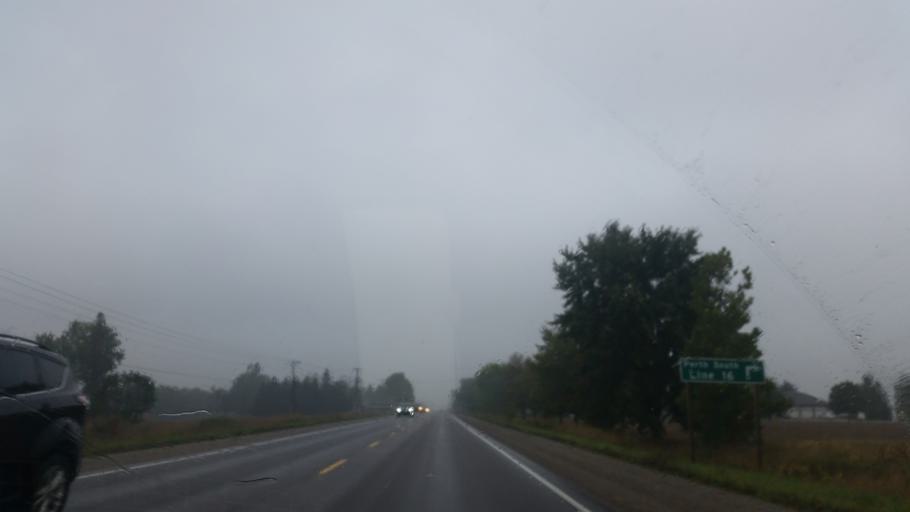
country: CA
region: Ontario
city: Stratford
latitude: 43.2959
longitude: -81.0461
